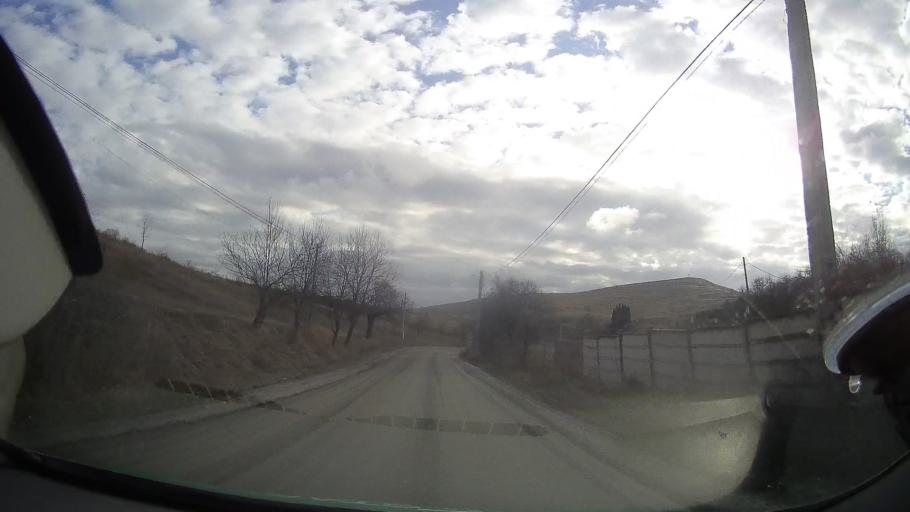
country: RO
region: Cluj
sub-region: Comuna Savadisla
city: Savadisla
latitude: 46.6431
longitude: 23.4629
